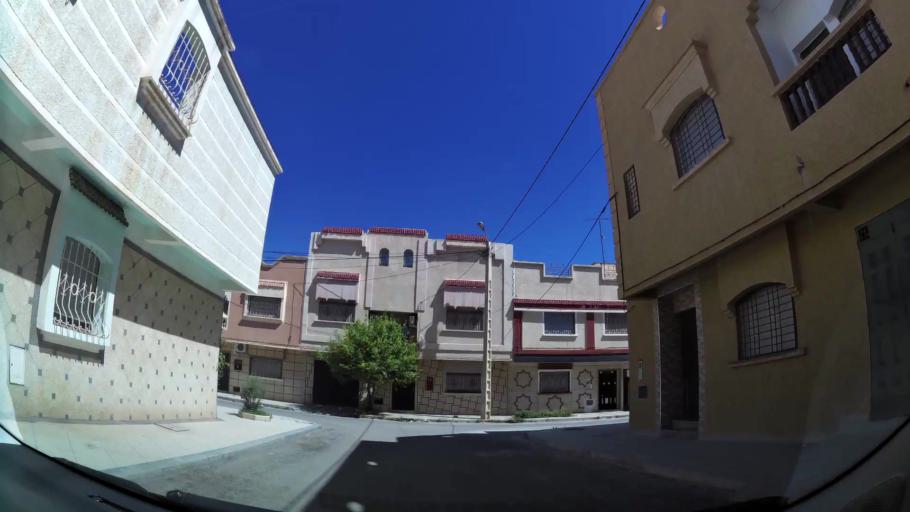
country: MA
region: Oriental
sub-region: Oujda-Angad
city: Oujda
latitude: 34.6644
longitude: -1.8889
